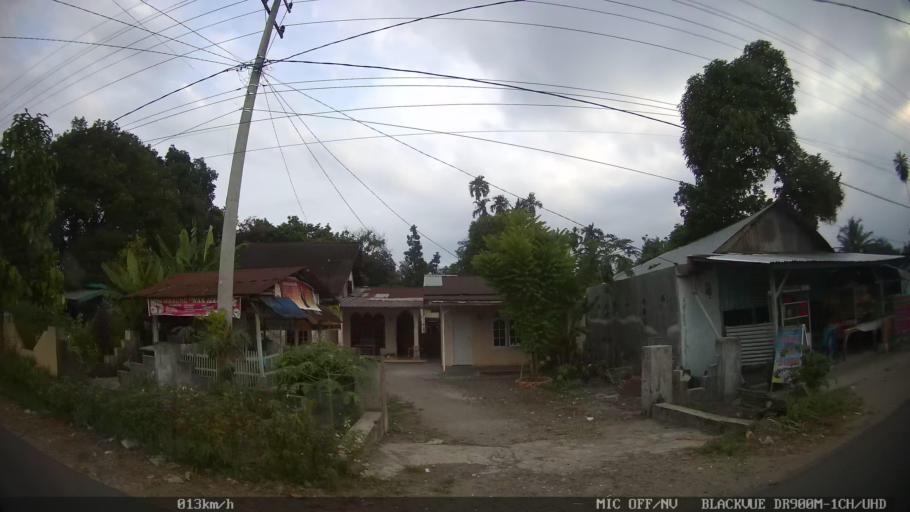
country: ID
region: North Sumatra
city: Sunggal
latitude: 3.5610
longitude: 98.5707
